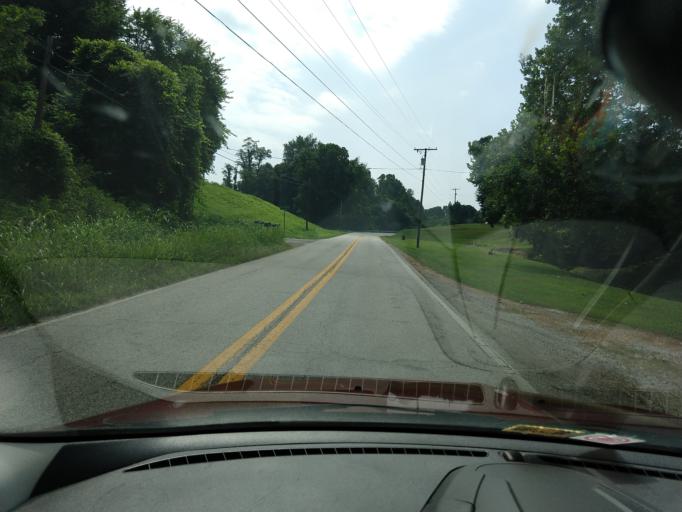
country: US
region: West Virginia
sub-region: Mason County
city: New Haven
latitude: 38.9357
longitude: -81.9185
